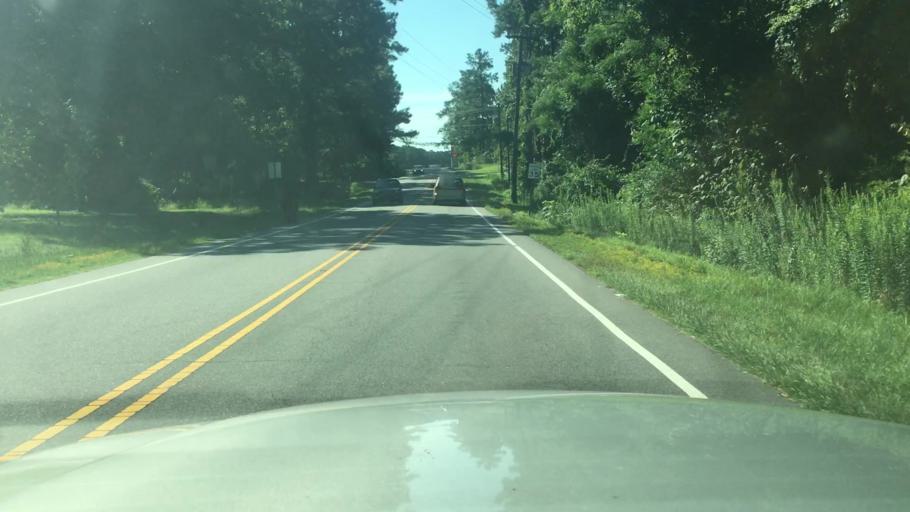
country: US
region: North Carolina
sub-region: Cumberland County
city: Fayetteville
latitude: 35.1150
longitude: -78.9082
